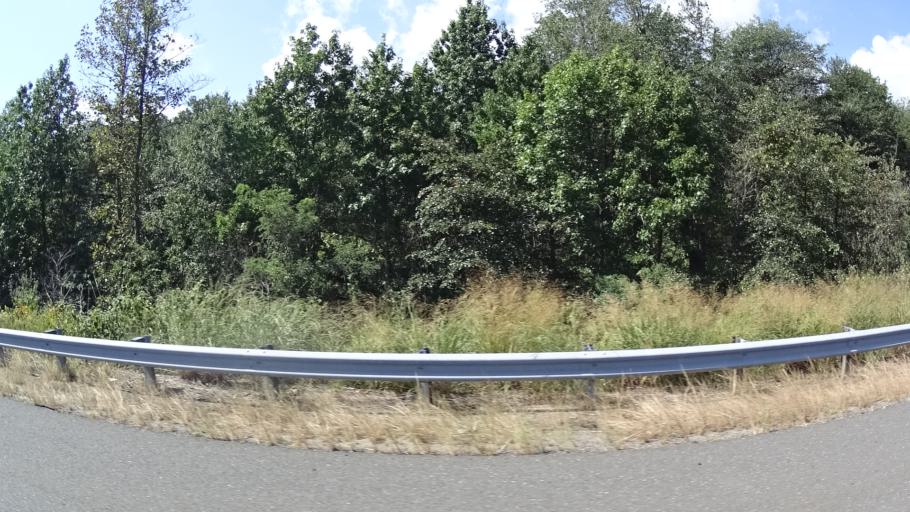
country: US
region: New Jersey
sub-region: Monmouth County
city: Eatontown
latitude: 40.2724
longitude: -74.0652
